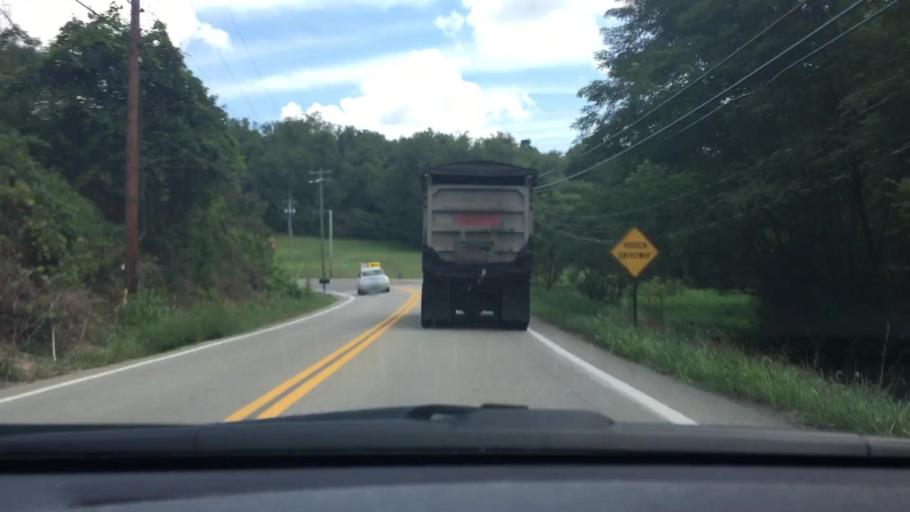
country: US
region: Pennsylvania
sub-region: Washington County
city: Gastonville
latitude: 40.2532
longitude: -79.9763
